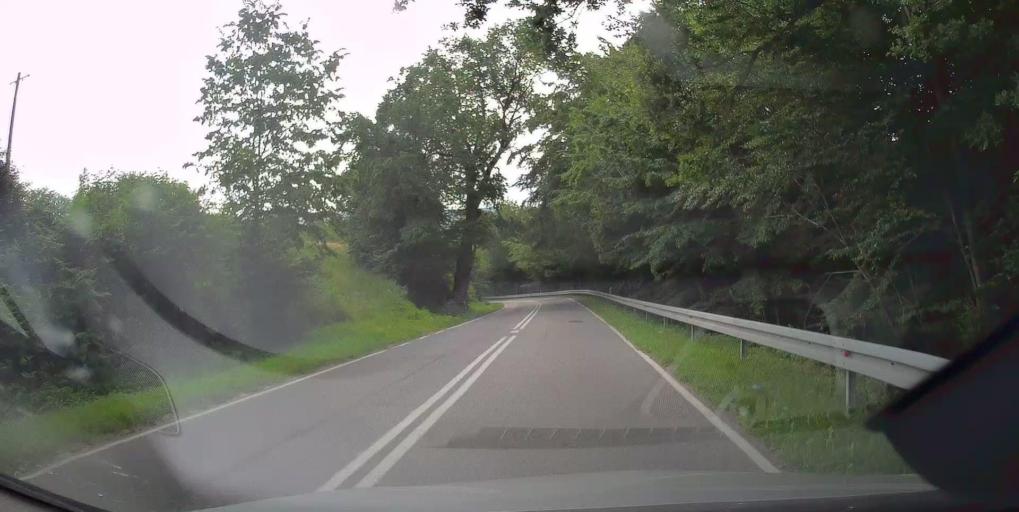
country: PL
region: Lesser Poland Voivodeship
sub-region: Powiat tarnowski
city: Zakliczyn
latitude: 49.7654
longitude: 20.7814
